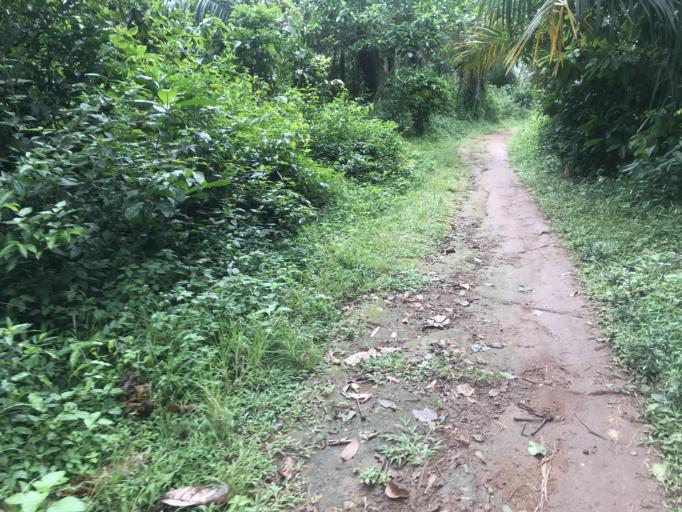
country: SL
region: Eastern Province
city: Buedu
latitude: 8.4640
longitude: -10.3068
